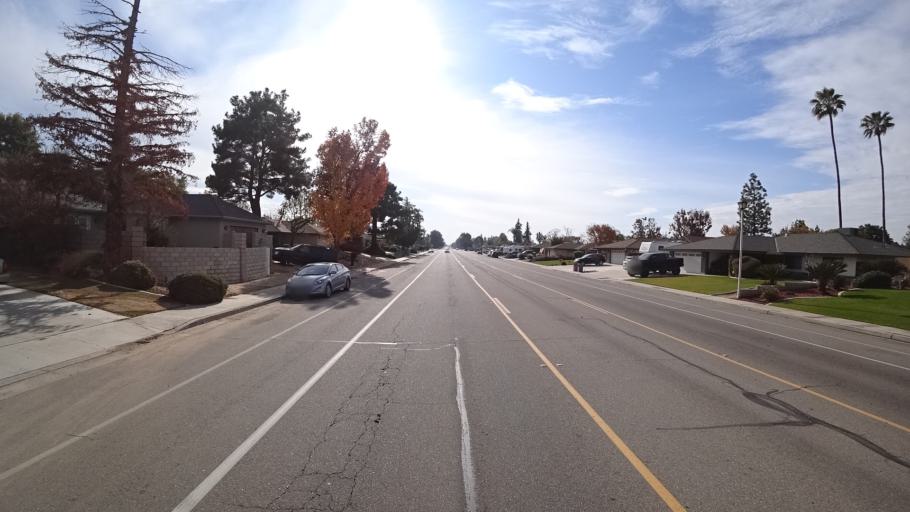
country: US
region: California
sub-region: Kern County
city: Greenacres
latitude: 35.4079
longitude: -119.0833
